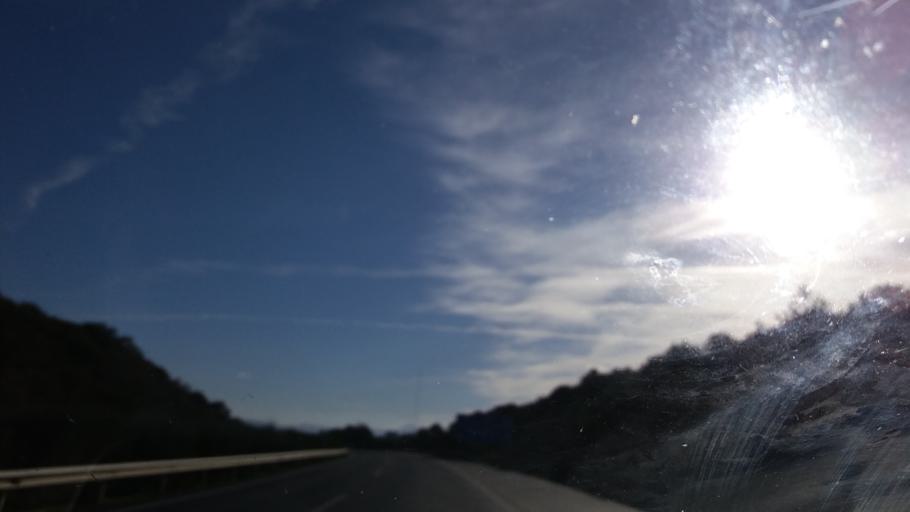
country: ES
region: Navarre
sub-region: Provincia de Navarra
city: Berriobeiti
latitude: 42.8504
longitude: -1.7083
